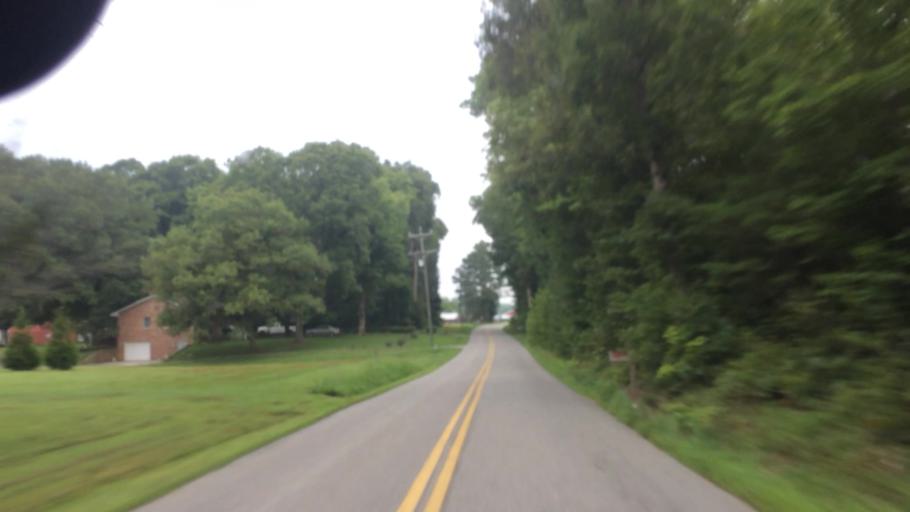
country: US
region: Virginia
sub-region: King William County
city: West Point
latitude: 37.5651
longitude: -76.7069
